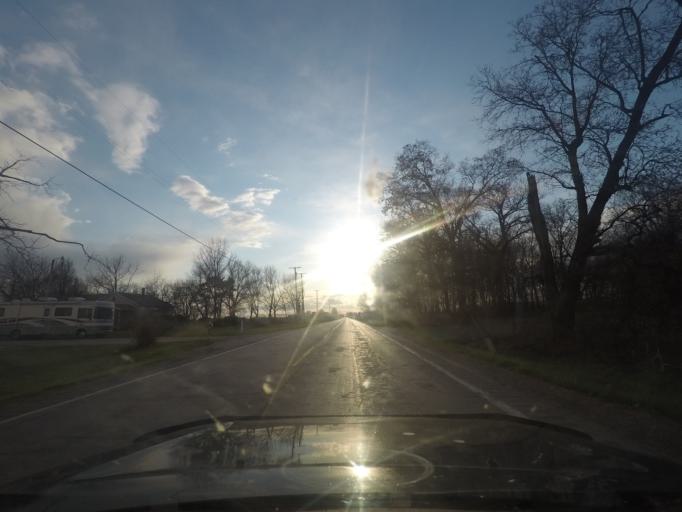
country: US
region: Indiana
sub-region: LaPorte County
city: Kingsford Heights
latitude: 41.5166
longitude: -86.7188
